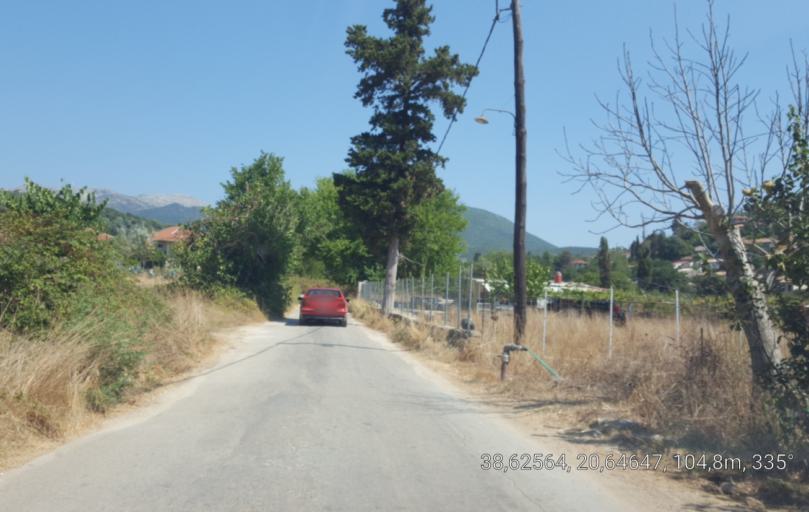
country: GR
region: Ionian Islands
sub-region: Lefkada
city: Nidri
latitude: 38.6256
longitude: 20.6464
